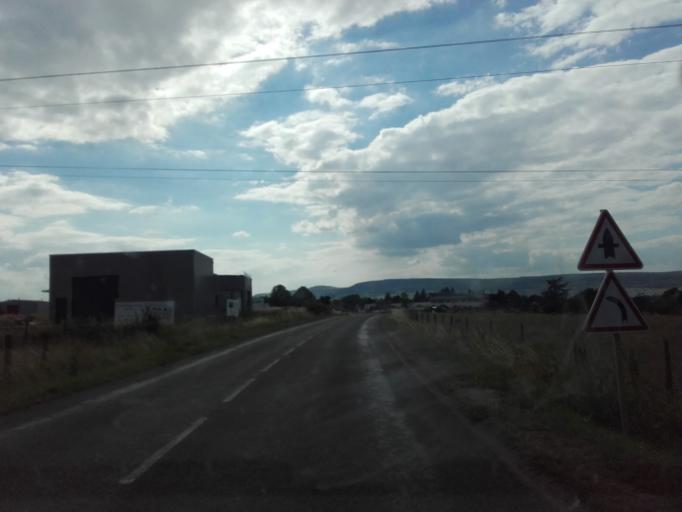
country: FR
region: Bourgogne
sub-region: Departement de Saone-et-Loire
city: Chagny
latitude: 46.9097
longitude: 4.7684
